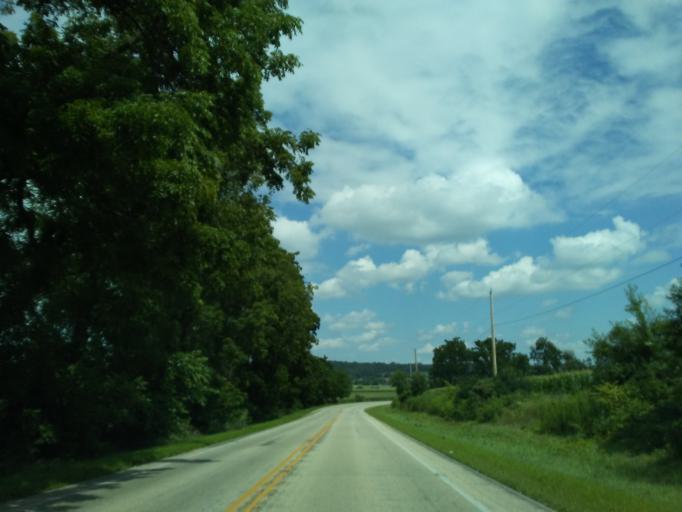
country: US
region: Wisconsin
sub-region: Dane County
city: Verona
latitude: 43.0124
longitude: -89.5752
